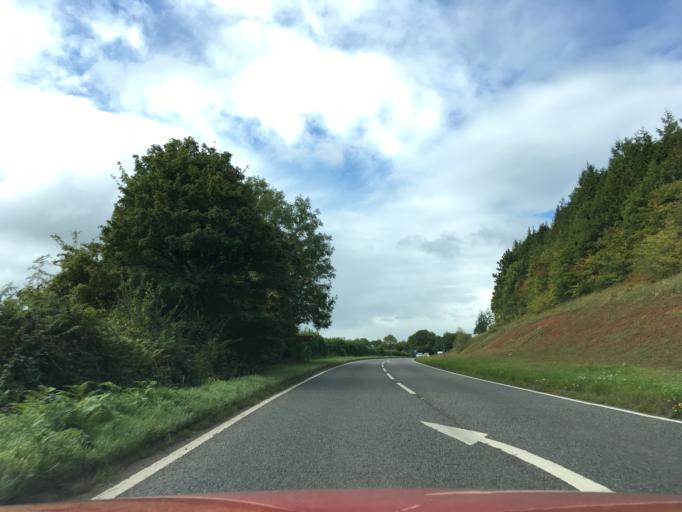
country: GB
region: Wales
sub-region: Monmouthshire
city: Chepstow
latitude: 51.6564
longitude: -2.6439
